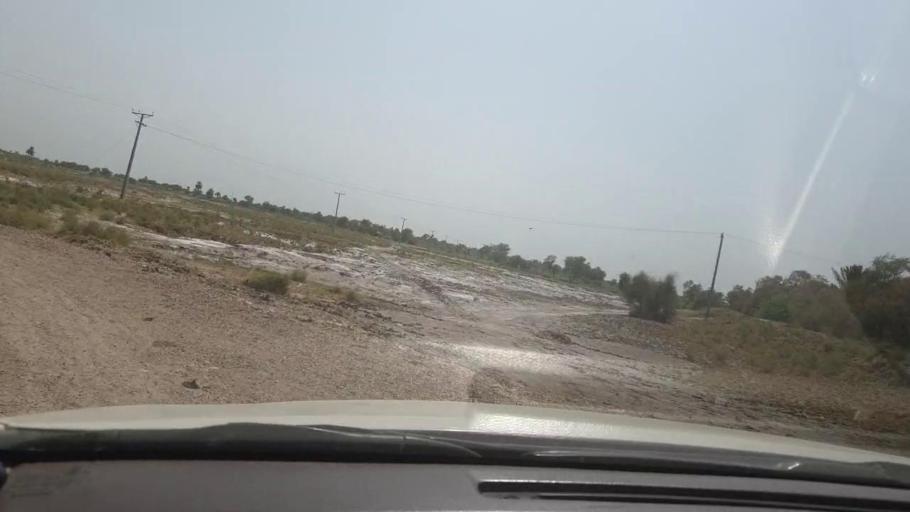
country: PK
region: Sindh
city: Shikarpur
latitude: 27.9233
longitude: 68.6058
